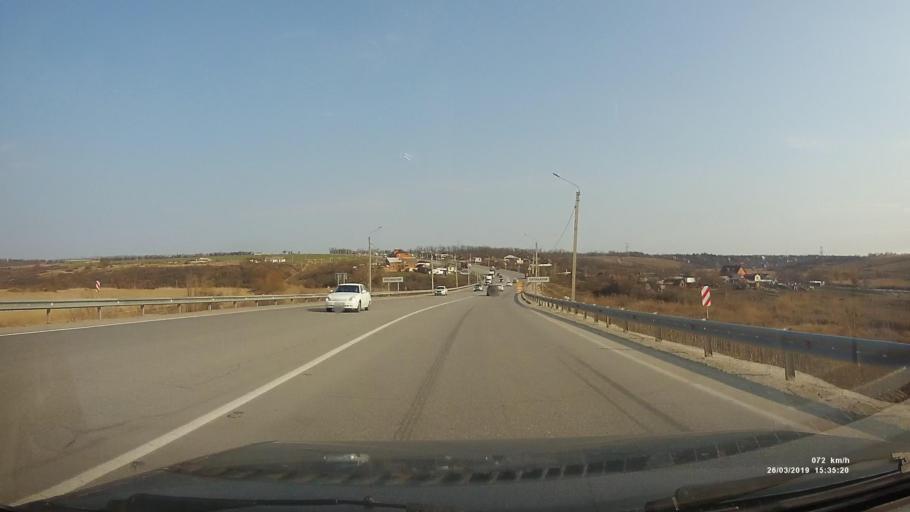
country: RU
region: Rostov
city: Sinyavskoye
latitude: 47.3004
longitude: 39.2112
